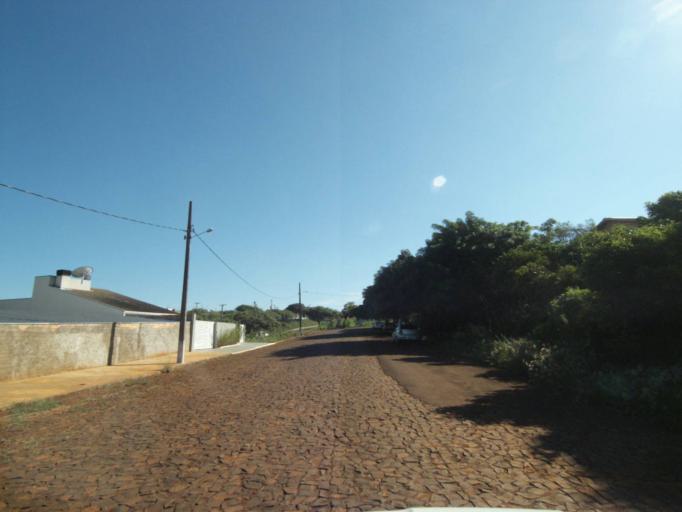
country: BR
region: Parana
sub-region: Laranjeiras Do Sul
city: Laranjeiras do Sul
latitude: -25.4884
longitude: -52.5253
